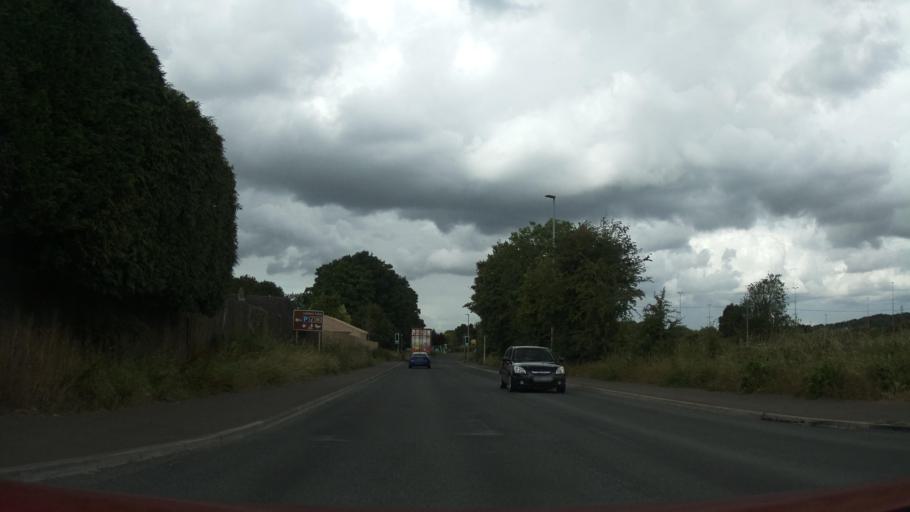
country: GB
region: England
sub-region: Wiltshire
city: Royal Wootton Bassett
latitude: 51.5518
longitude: -1.8945
